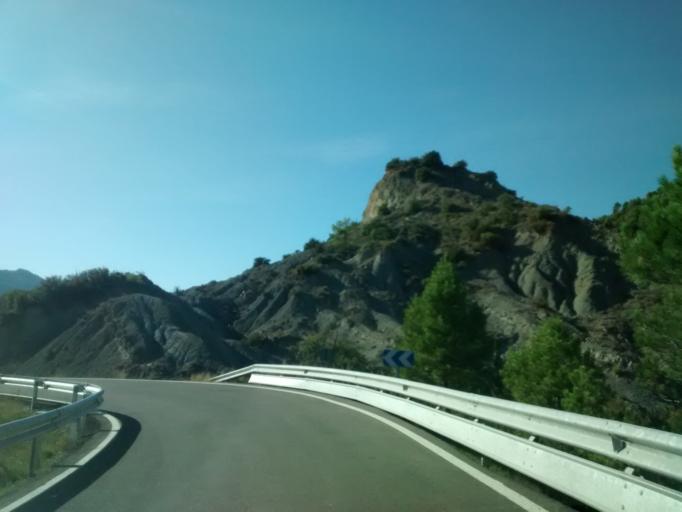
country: ES
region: Aragon
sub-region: Provincia de Huesca
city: Loarre
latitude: 42.3877
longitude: -0.7044
